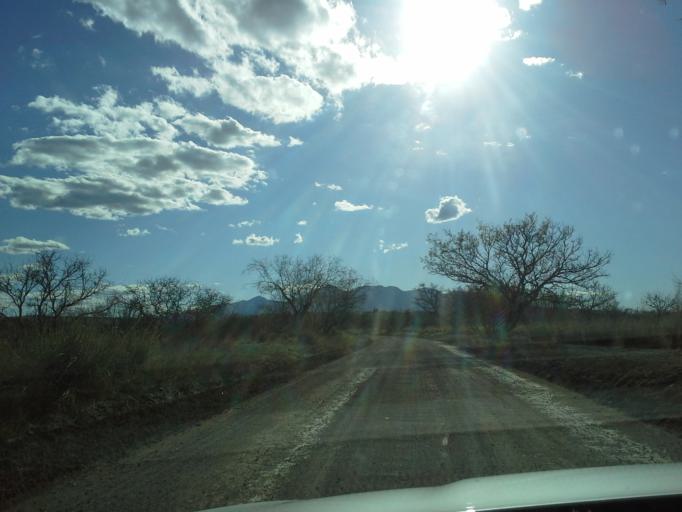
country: US
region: Arizona
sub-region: Pima County
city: Corona de Tucson
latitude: 31.7363
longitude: -110.6715
